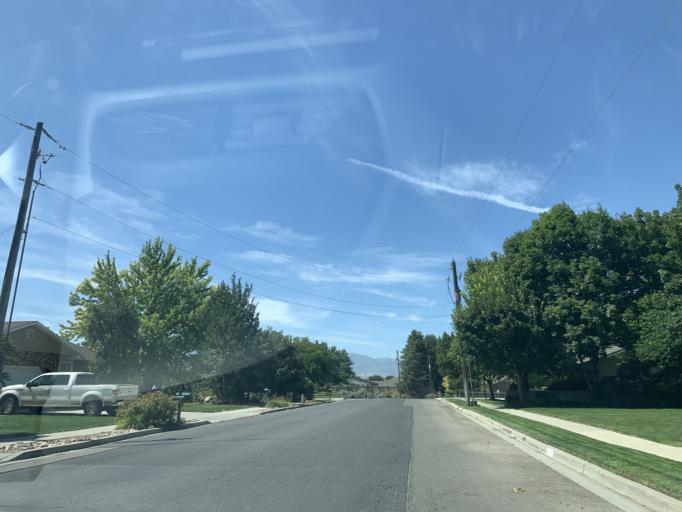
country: US
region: Utah
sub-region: Utah County
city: Lehi
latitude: 40.4062
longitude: -111.8287
